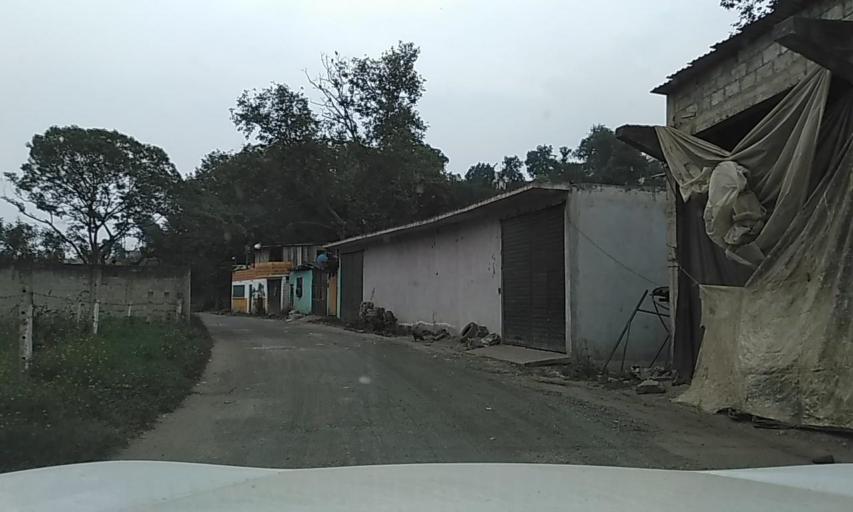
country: MX
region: Veracruz
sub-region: Jilotepec
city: El Pueblito (Garbanzal)
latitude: 19.5718
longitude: -96.8931
